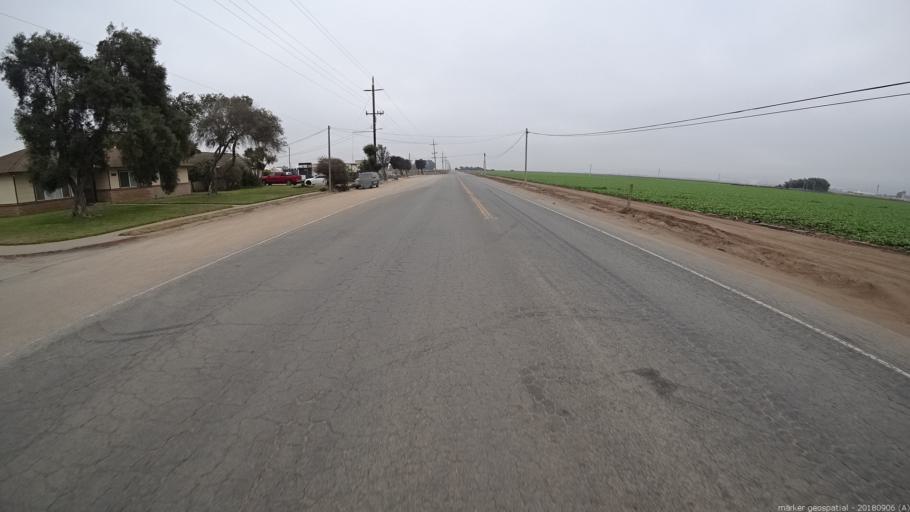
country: US
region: California
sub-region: Monterey County
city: Salinas
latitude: 36.6714
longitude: -121.5997
